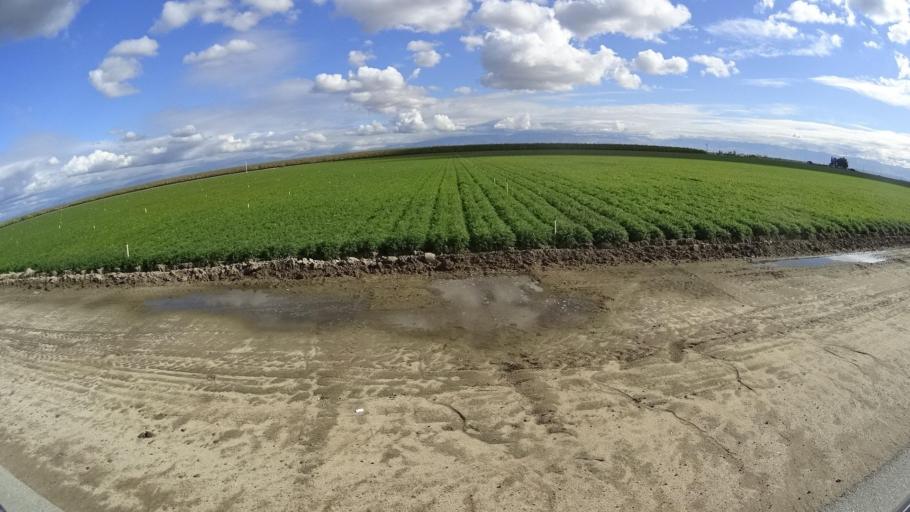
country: US
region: California
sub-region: Kern County
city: Greenfield
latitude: 35.2186
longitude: -119.0744
